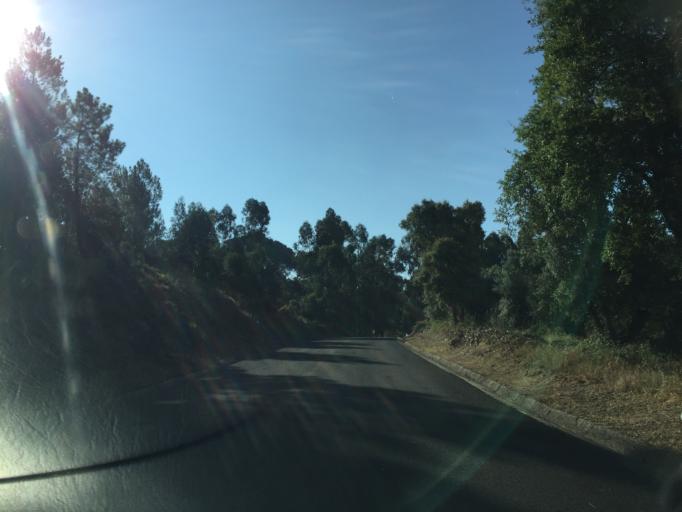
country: PT
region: Santarem
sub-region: Abrantes
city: Alferrarede
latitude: 39.5219
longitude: -8.1451
